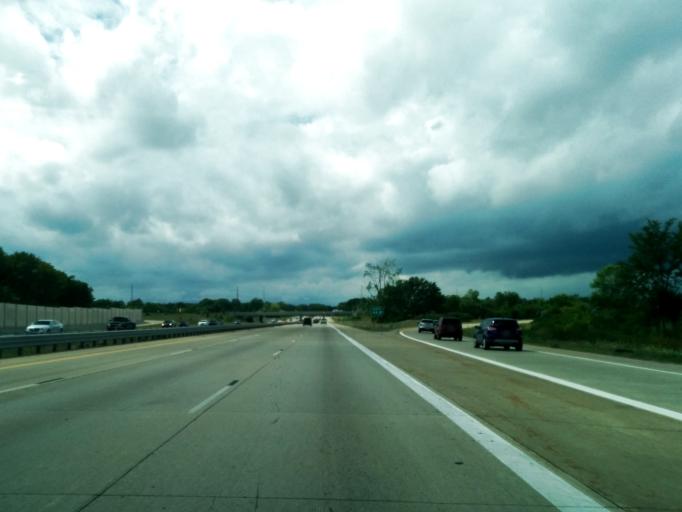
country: US
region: Michigan
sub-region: Oakland County
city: Troy
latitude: 42.6268
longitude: -83.1253
